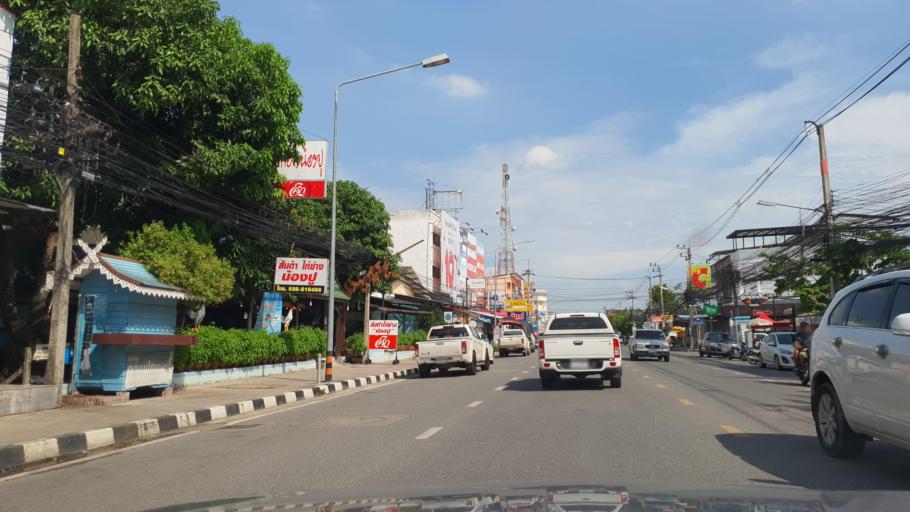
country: TH
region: Chachoengsao
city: Chachoengsao
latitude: 13.6835
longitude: 101.0664
